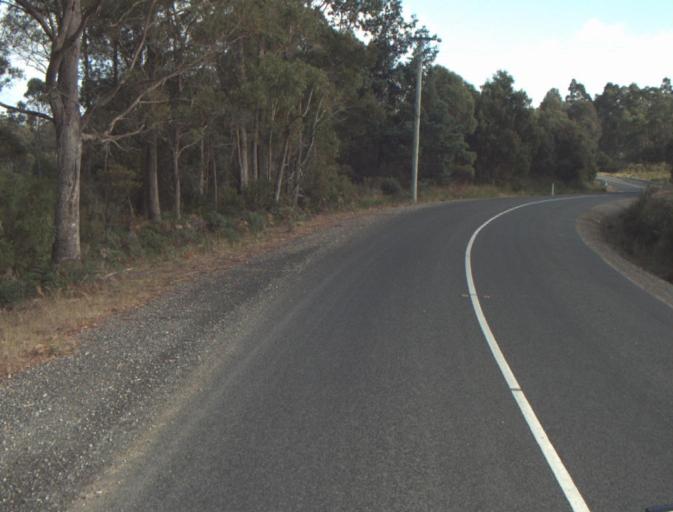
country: AU
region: Tasmania
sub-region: Dorset
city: Bridport
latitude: -41.1413
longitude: 147.2279
